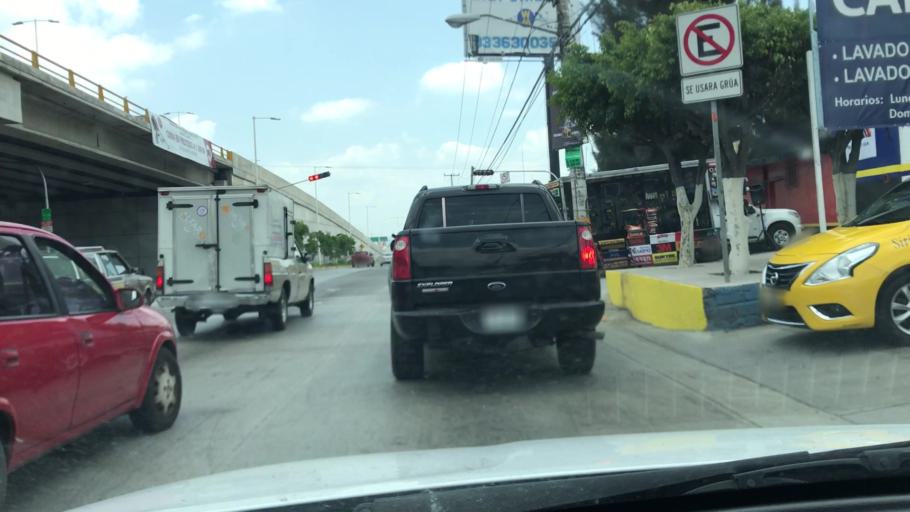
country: MX
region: Jalisco
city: Zapopan2
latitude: 20.7276
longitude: -103.4154
